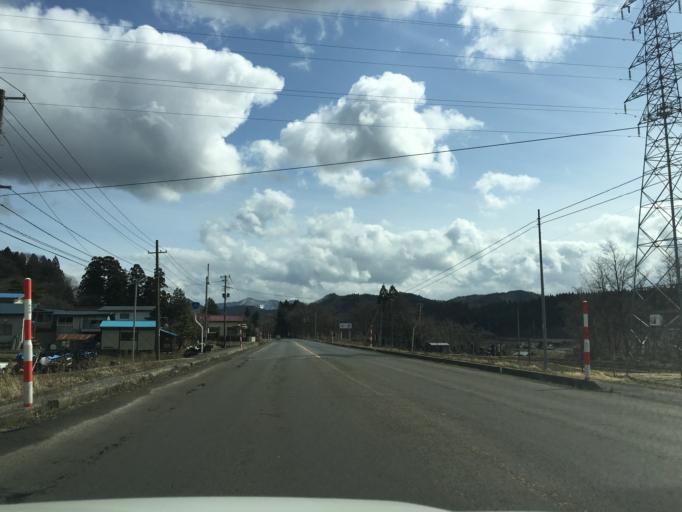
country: JP
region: Akita
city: Odate
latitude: 40.2268
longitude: 140.5999
